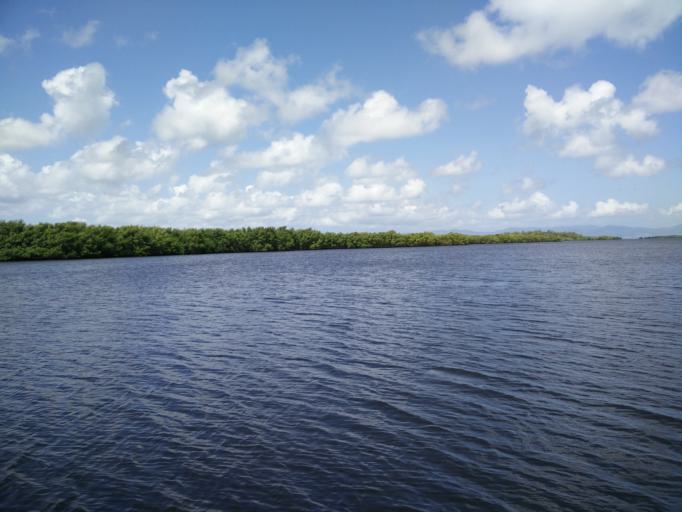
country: GP
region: Guadeloupe
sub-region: Guadeloupe
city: Petit-Canal
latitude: 16.3542
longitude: -61.4954
